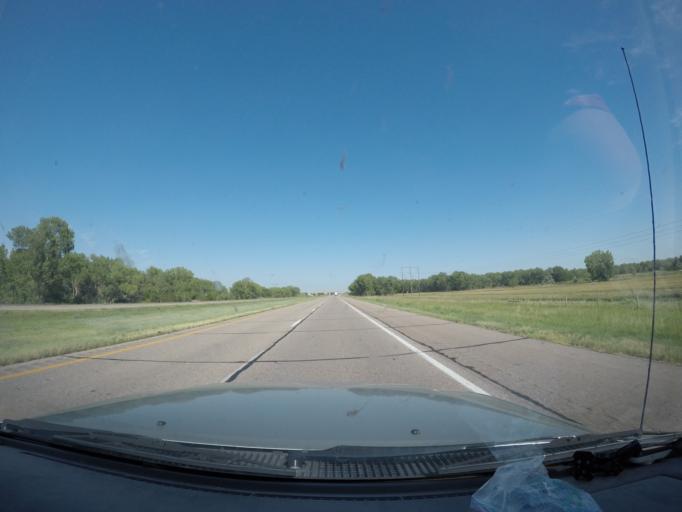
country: US
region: Nebraska
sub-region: Buffalo County
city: Kearney
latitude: 40.6817
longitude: -99.2944
